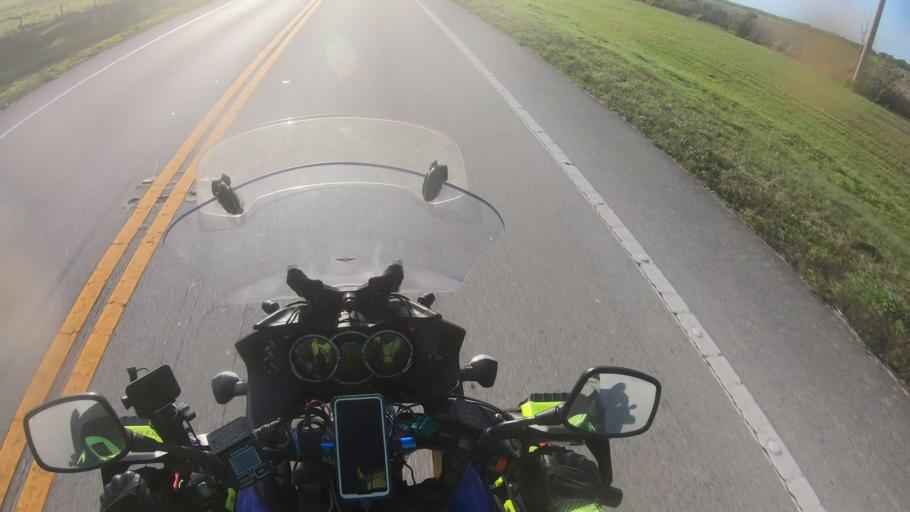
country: US
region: Florida
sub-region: DeSoto County
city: Southeast Arcadia
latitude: 27.2083
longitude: -81.7440
